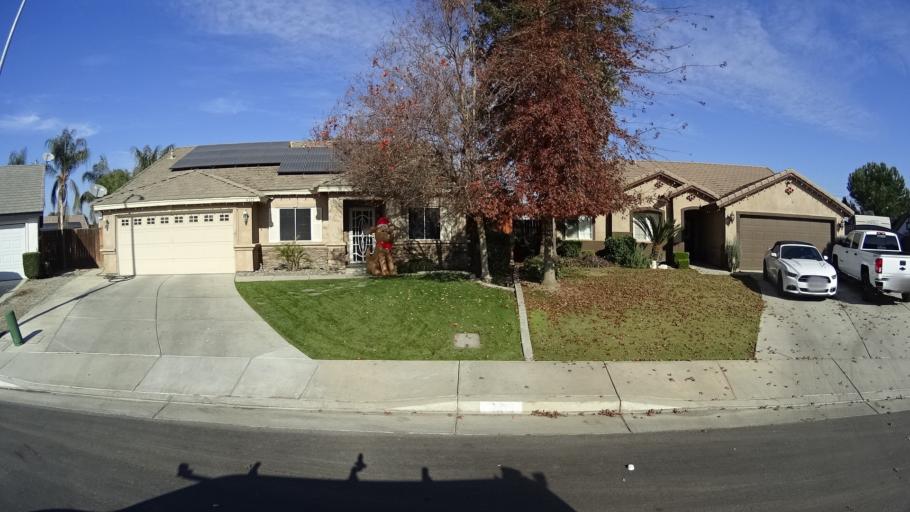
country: US
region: California
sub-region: Kern County
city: Greenacres
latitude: 35.3992
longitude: -119.0948
